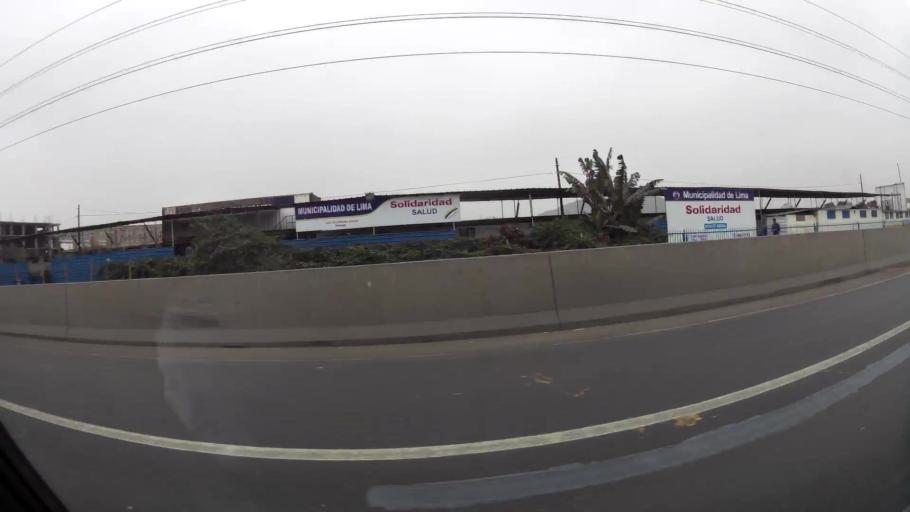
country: PE
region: Lima
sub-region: Lima
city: Carabayllo
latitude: -11.8712
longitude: -77.0701
